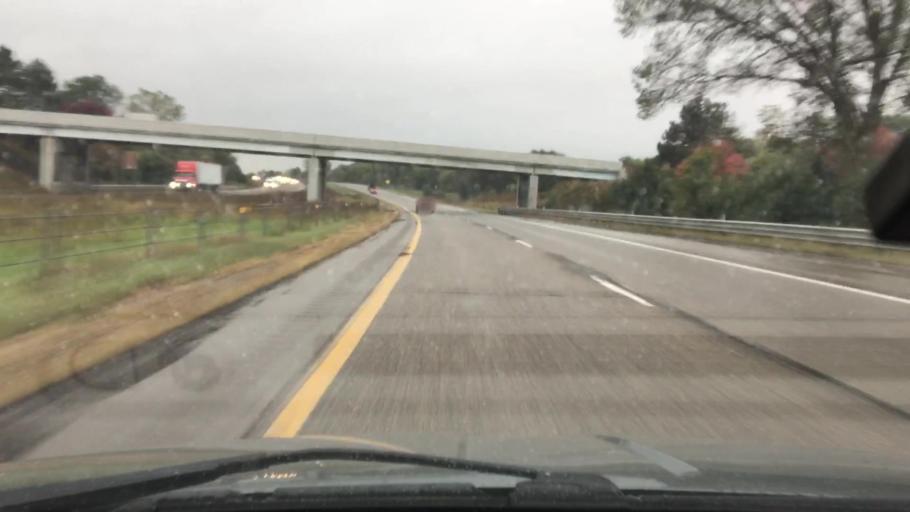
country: US
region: Michigan
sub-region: Washtenaw County
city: Chelsea
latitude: 42.2972
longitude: -84.0925
